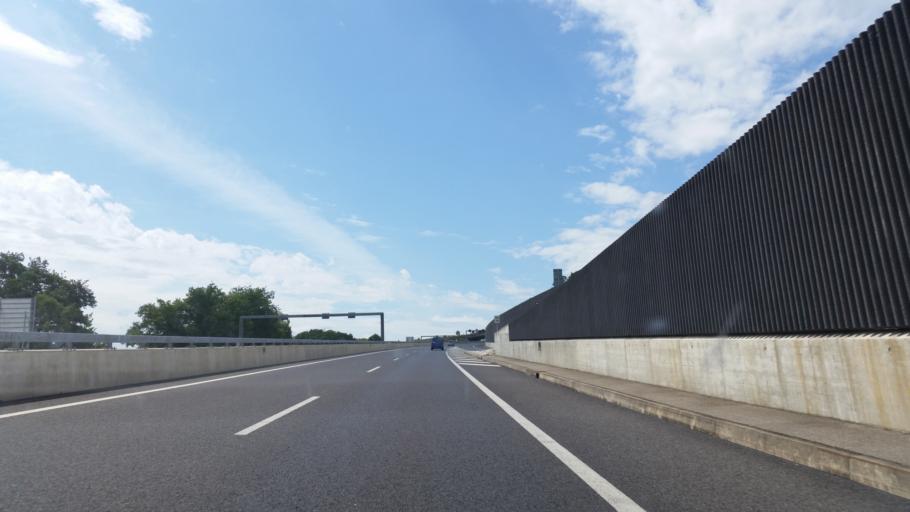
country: CH
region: Neuchatel
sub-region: Boudry District
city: Saint-Aubin-Sauges
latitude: 46.8707
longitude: 6.7541
